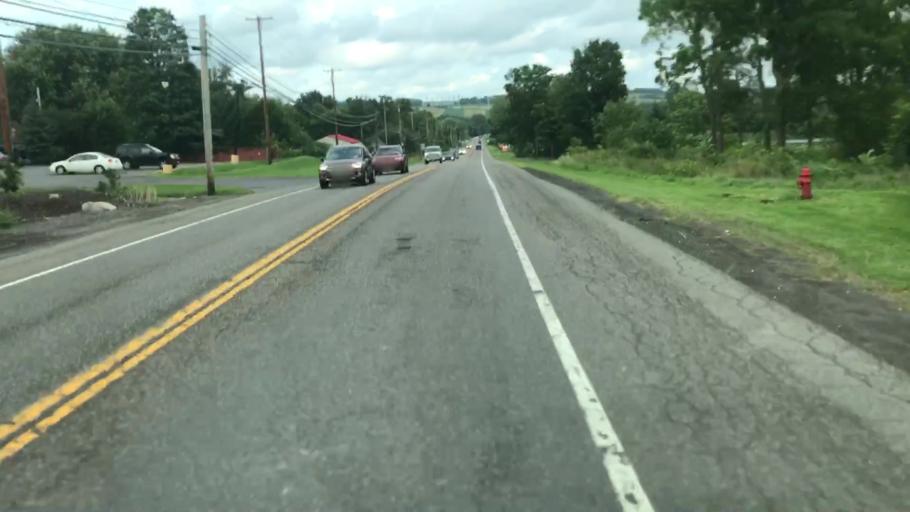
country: US
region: New York
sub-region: Onondaga County
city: Elbridge
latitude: 43.0379
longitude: -76.4243
